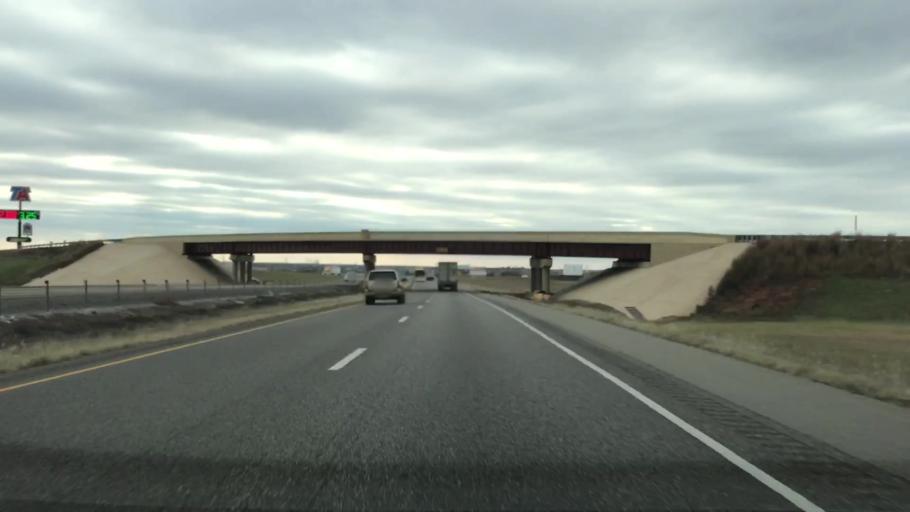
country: US
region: Oklahoma
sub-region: Beckham County
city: Sayre
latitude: 35.3385
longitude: -99.5928
